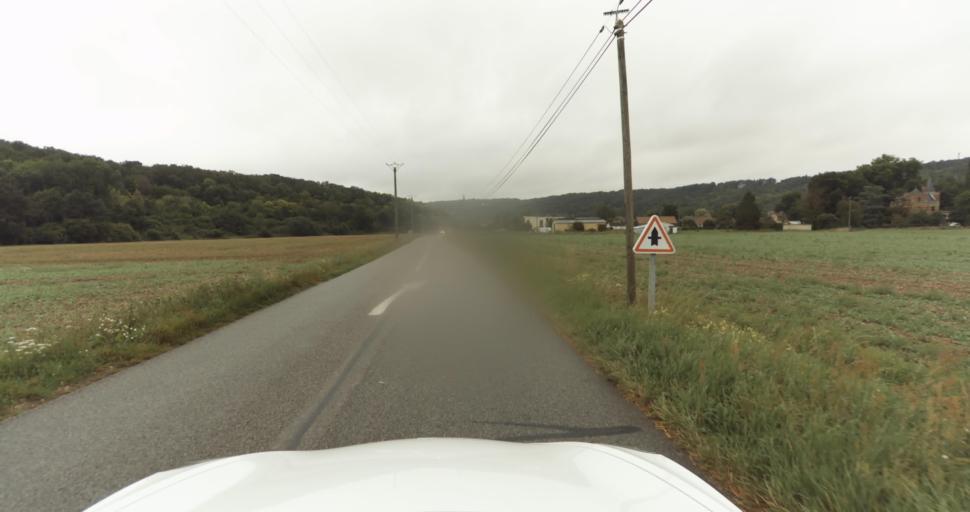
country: FR
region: Haute-Normandie
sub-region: Departement de l'Eure
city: Normanville
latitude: 49.0878
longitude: 1.1384
